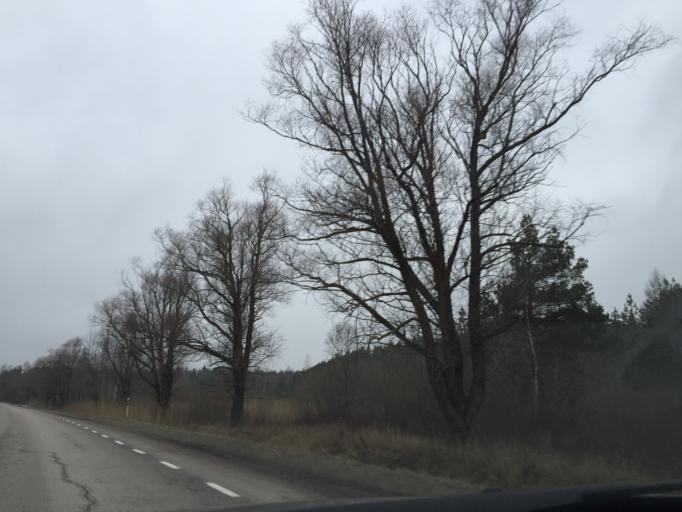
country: EE
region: Saare
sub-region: Kuressaare linn
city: Kuressaare
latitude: 58.2741
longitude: 22.4532
